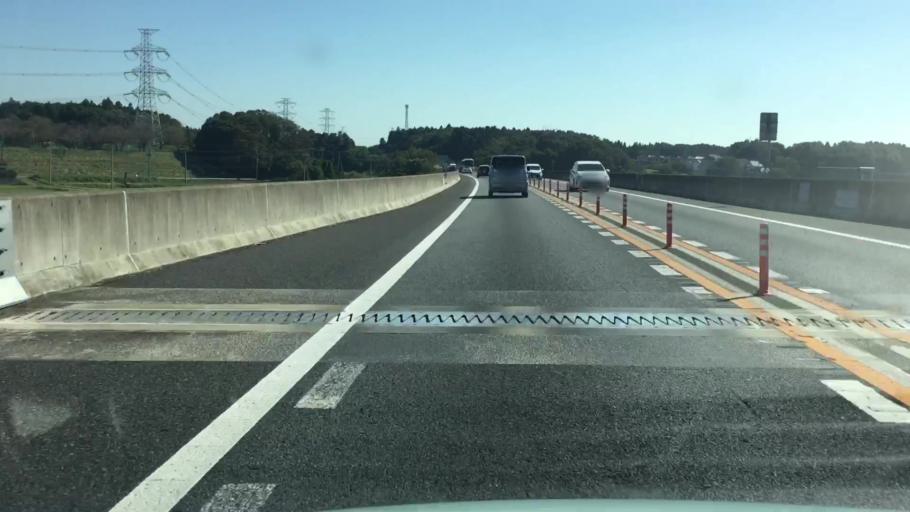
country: JP
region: Ibaraki
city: Ushiku
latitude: 35.9932
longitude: 140.1619
